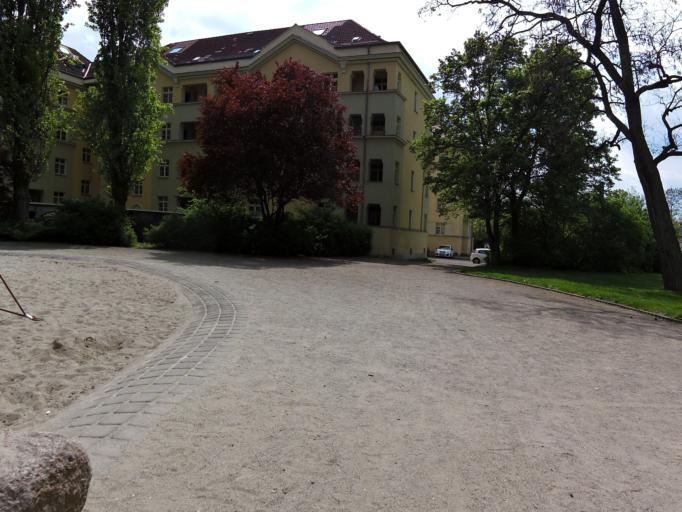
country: DE
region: Saxony
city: Leipzig
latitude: 51.3605
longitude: 12.3875
